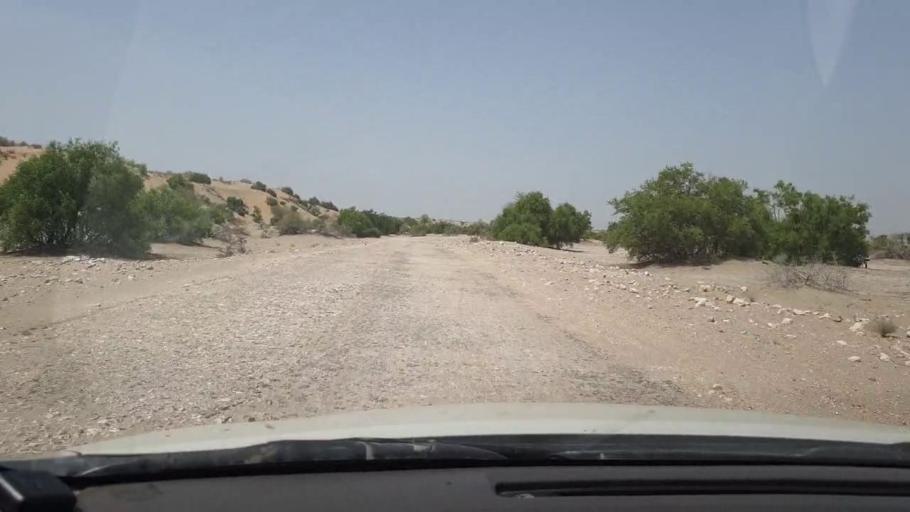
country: PK
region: Sindh
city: Rohri
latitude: 27.2942
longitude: 69.2696
